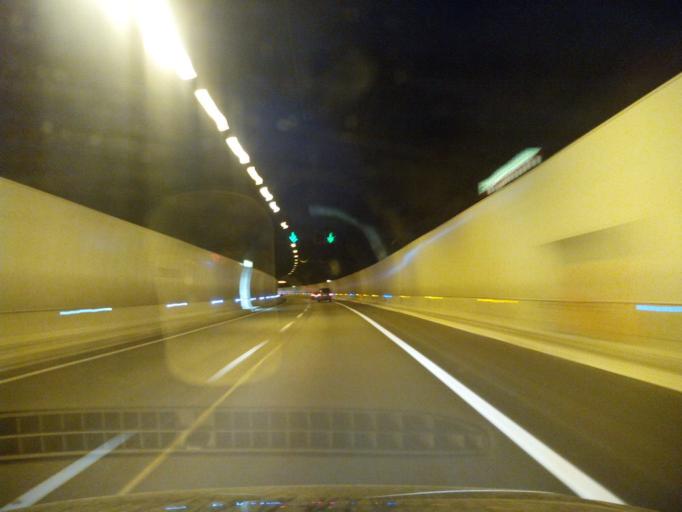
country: ES
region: Catalonia
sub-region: Provincia de Barcelona
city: Gironella
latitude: 42.0019
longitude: 1.8801
